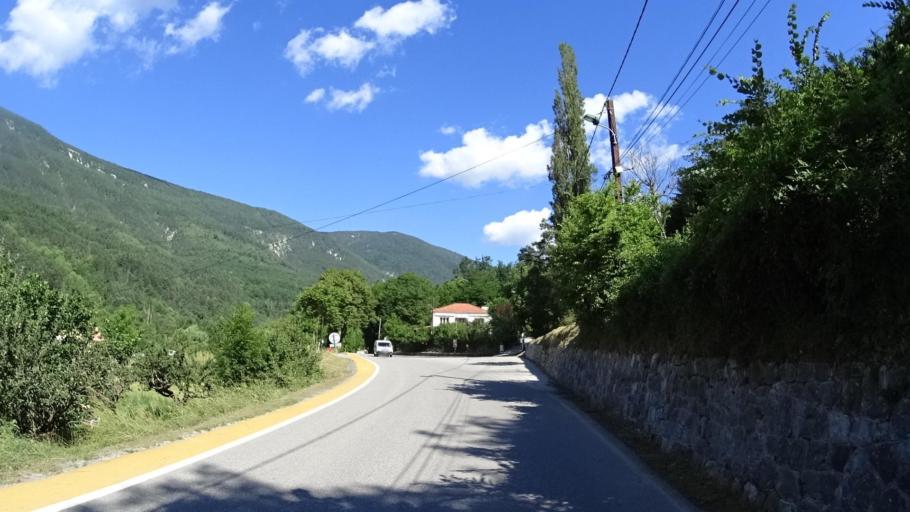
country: FR
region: Provence-Alpes-Cote d'Azur
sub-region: Departement des Alpes-de-Haute-Provence
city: Annot
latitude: 43.9706
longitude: 6.6608
